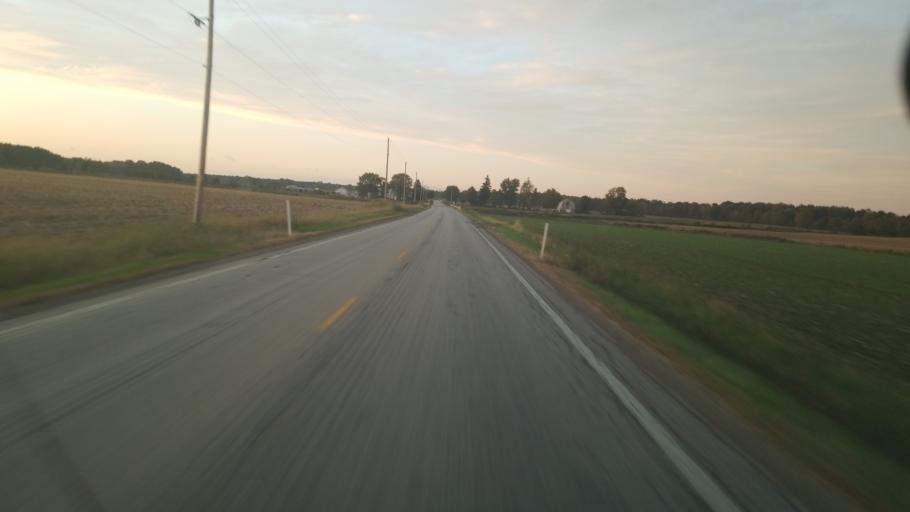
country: US
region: Ohio
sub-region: Ashtabula County
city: Andover
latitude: 41.6609
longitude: -80.6671
